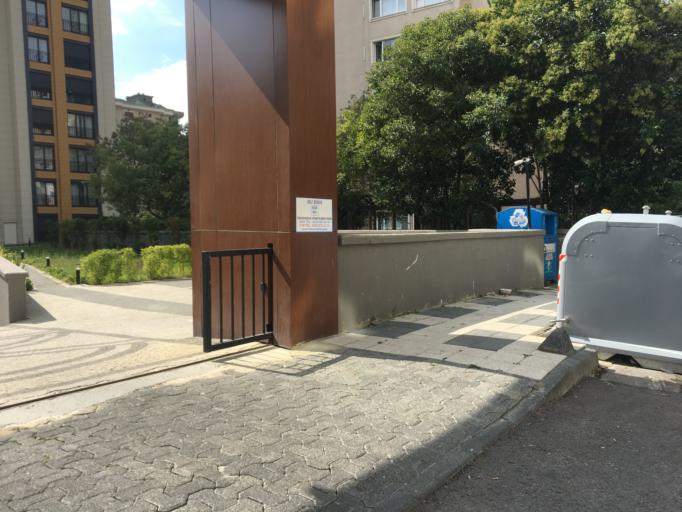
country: TR
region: Istanbul
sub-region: Atasehir
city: Atasehir
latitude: 40.9649
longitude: 29.0982
